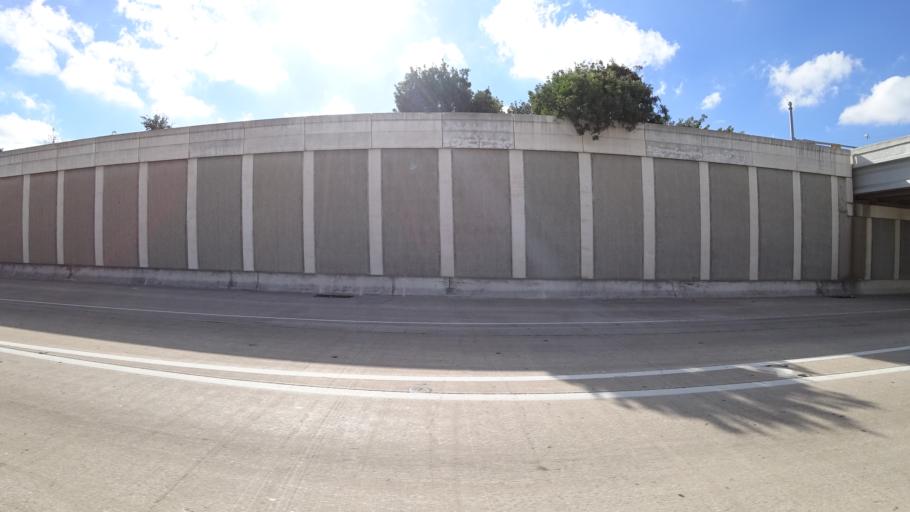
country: US
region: Texas
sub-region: Travis County
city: Austin
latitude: 30.2160
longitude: -97.7436
